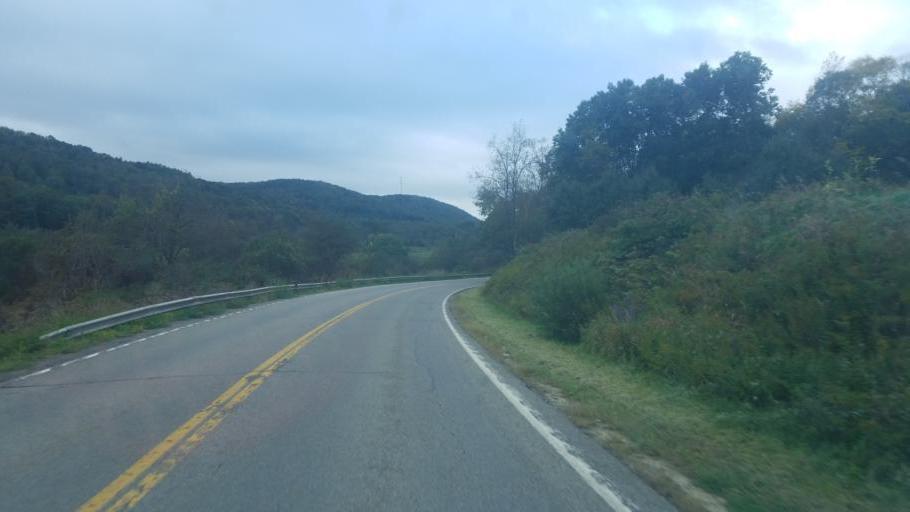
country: US
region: New York
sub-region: Allegany County
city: Cuba
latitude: 42.1835
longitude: -78.3597
